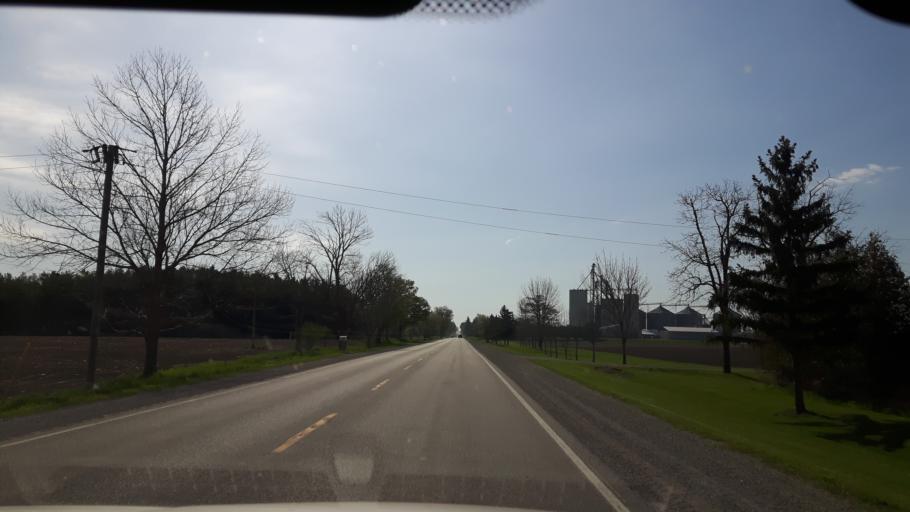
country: CA
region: Ontario
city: Bluewater
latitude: 43.5378
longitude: -81.6141
